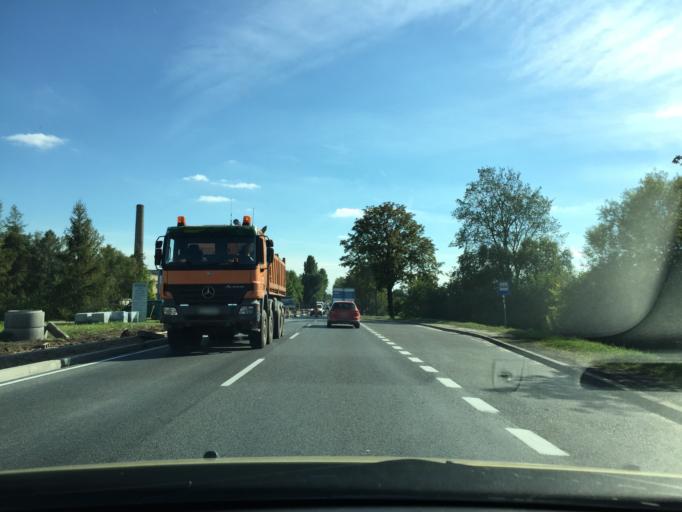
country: PL
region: Greater Poland Voivodeship
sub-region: Kalisz
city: Kalisz
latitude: 51.7950
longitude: 18.0913
